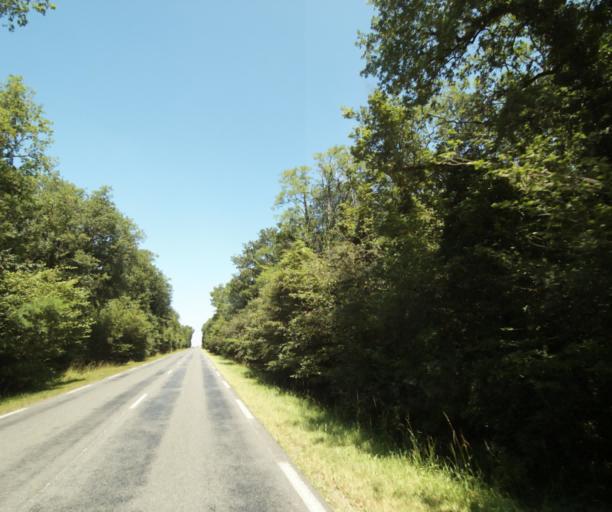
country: FR
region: Centre
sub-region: Departement du Loiret
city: Malesherbes
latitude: 48.3143
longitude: 2.4393
